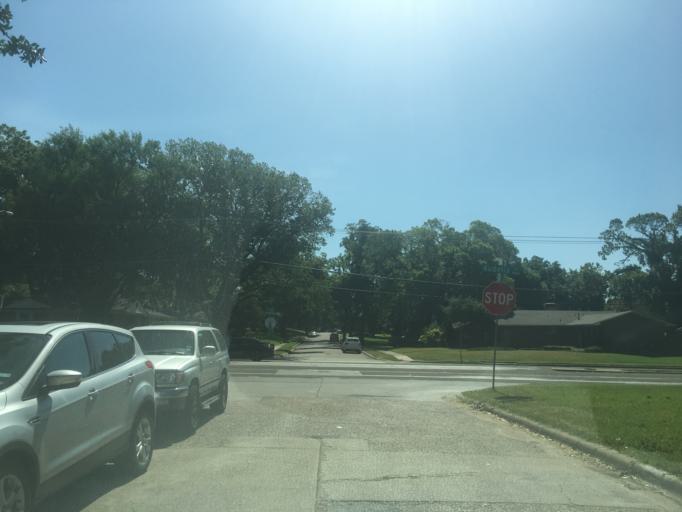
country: US
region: Texas
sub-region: Dallas County
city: Richardson
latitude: 32.8688
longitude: -96.7189
